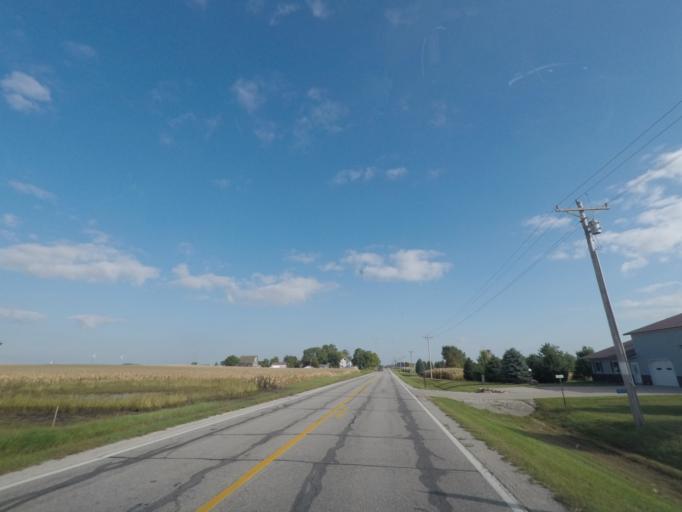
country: US
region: Iowa
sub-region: Story County
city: Nevada
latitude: 41.9981
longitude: -93.4628
